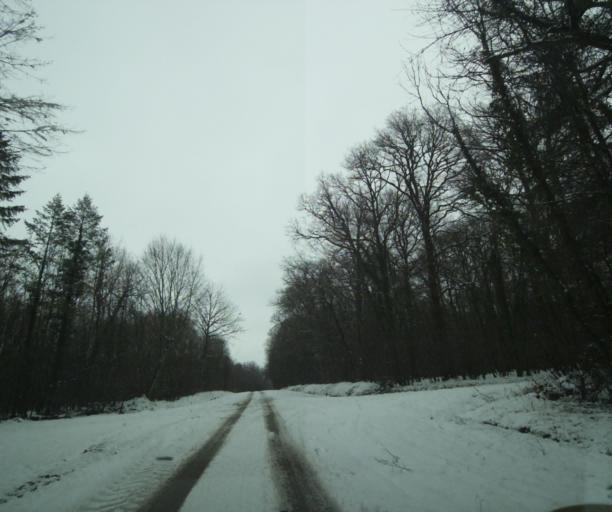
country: FR
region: Champagne-Ardenne
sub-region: Departement de la Haute-Marne
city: Montier-en-Der
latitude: 48.4208
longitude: 4.7739
